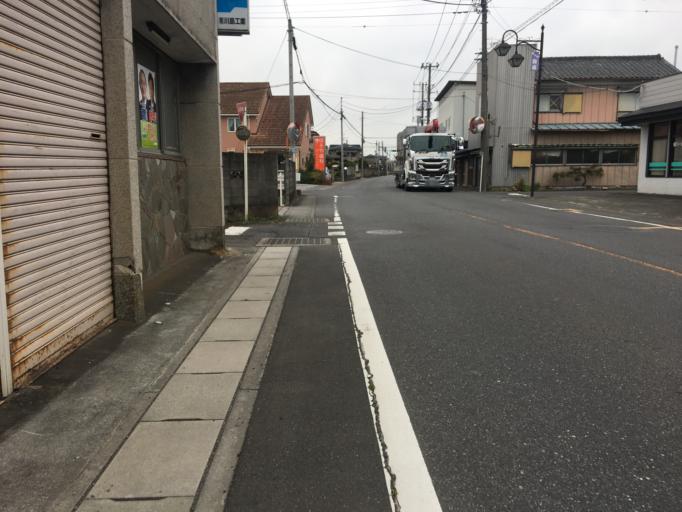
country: JP
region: Saitama
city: Kisai
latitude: 36.1014
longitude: 139.5814
